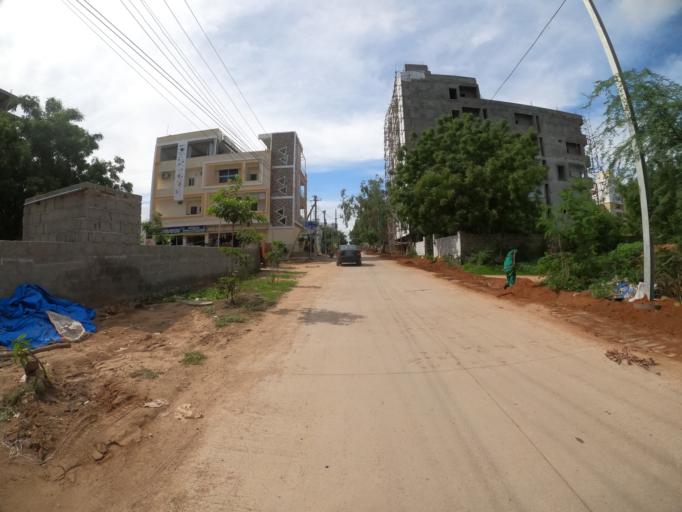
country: IN
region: Telangana
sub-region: Hyderabad
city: Hyderabad
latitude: 17.3562
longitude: 78.3949
